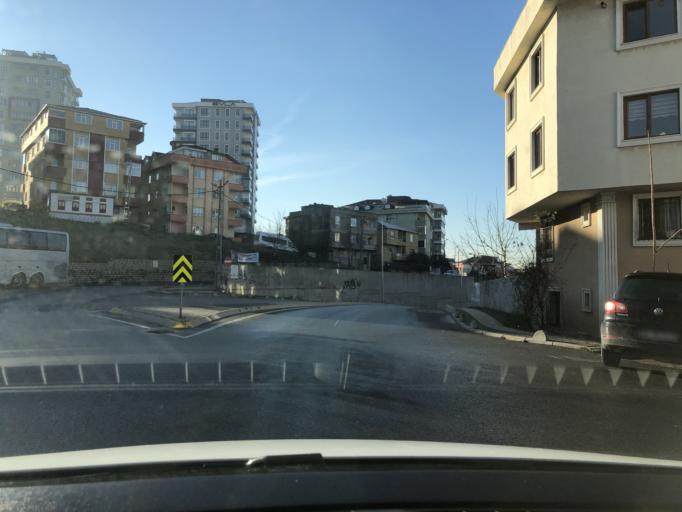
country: TR
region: Istanbul
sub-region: Atasehir
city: Atasehir
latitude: 40.9768
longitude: 29.1270
